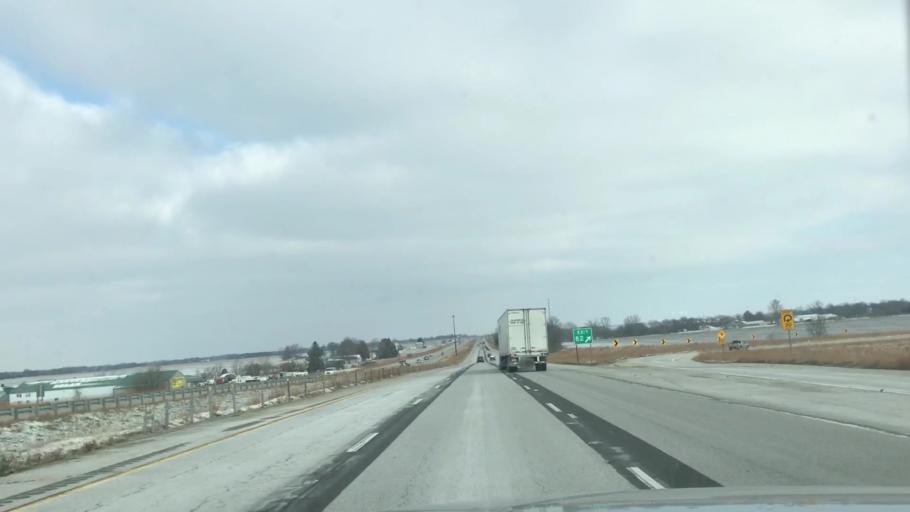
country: US
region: Illinois
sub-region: Sangamon County
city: Divernon
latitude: 39.5911
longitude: -89.6464
